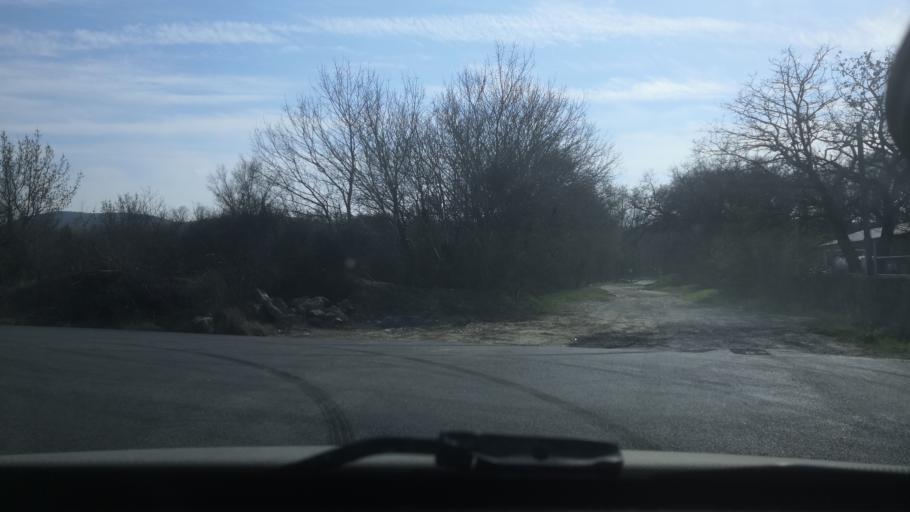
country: FR
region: Rhone-Alpes
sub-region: Departement de la Drome
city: Montboucher-sur-Jabron
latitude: 44.5456
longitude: 4.7886
